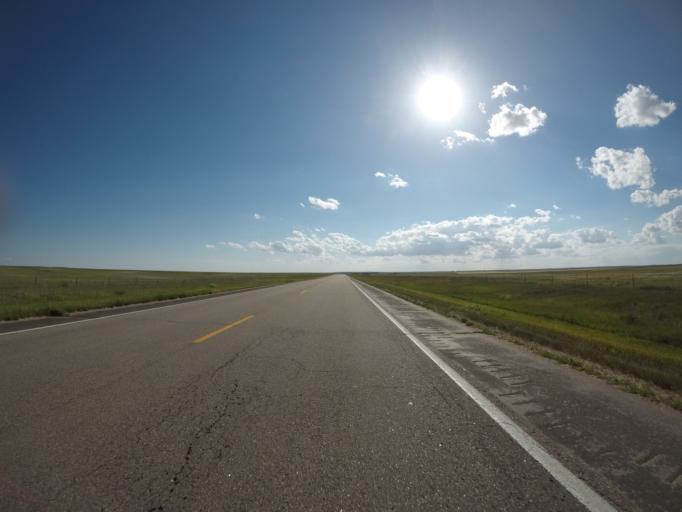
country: US
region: Colorado
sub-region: Morgan County
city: Fort Morgan
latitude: 40.5990
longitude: -103.8720
